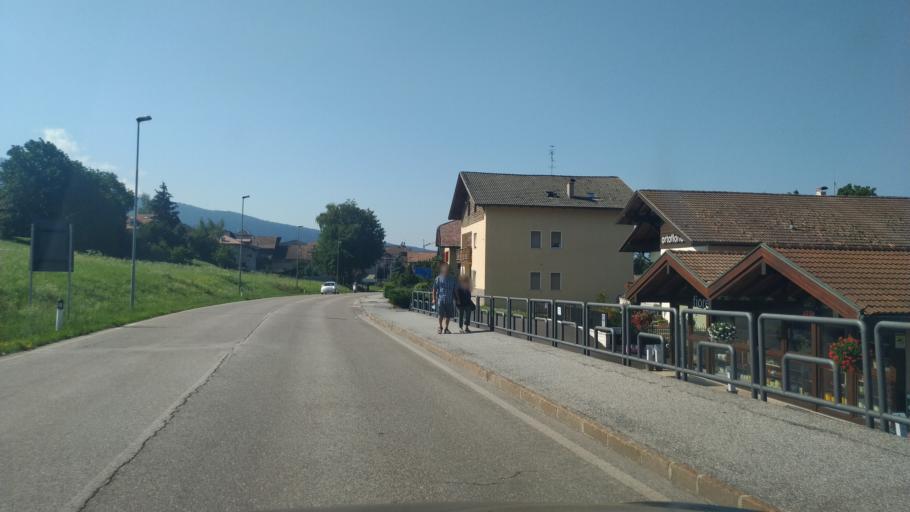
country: IT
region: Trentino-Alto Adige
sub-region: Provincia di Trento
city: Sarnonico
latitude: 46.4230
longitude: 11.1413
